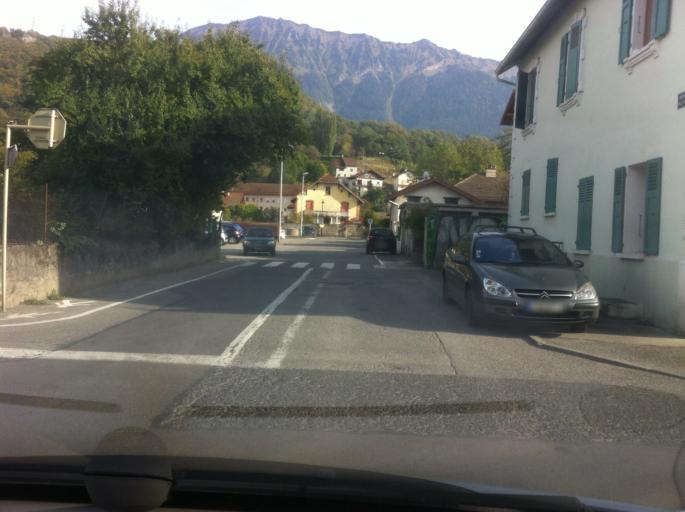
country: FR
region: Rhone-Alpes
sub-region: Departement de la Haute-Savoie
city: Faverges
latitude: 45.7452
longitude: 6.2931
